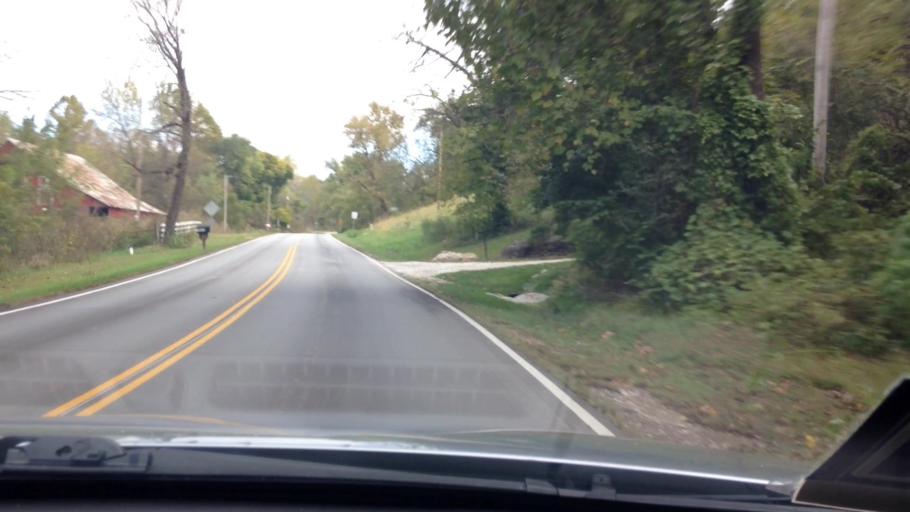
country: US
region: Missouri
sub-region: Platte County
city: Weatherby Lake
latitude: 39.2456
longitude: -94.7970
